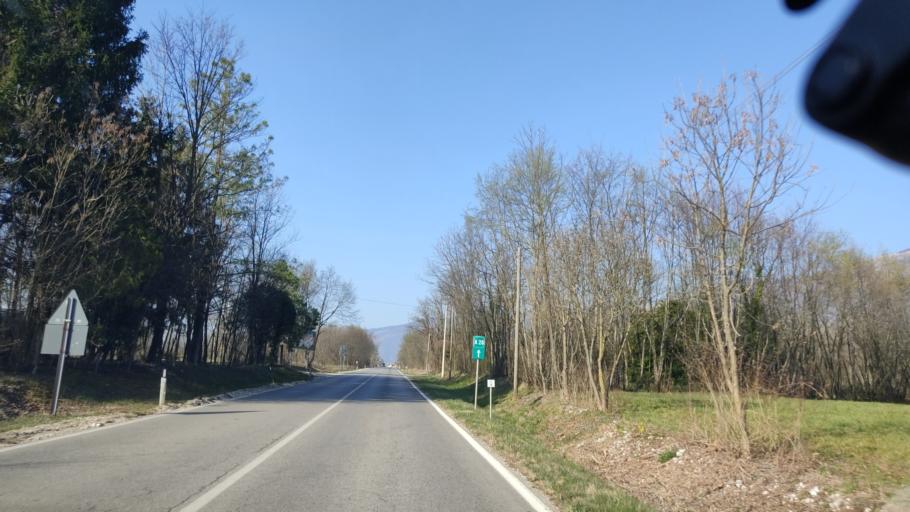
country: IT
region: Friuli Venezia Giulia
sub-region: Provincia di Pordenone
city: Budoia
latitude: 46.0568
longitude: 12.5529
